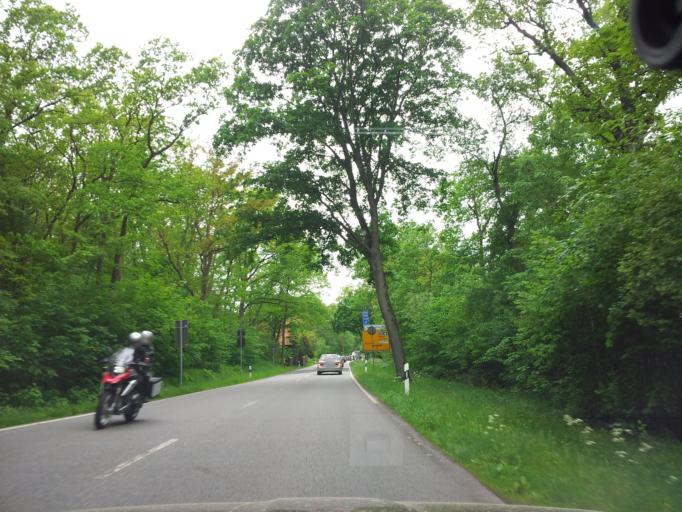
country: DE
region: Brandenburg
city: Brieselang
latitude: 52.6144
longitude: 13.0097
